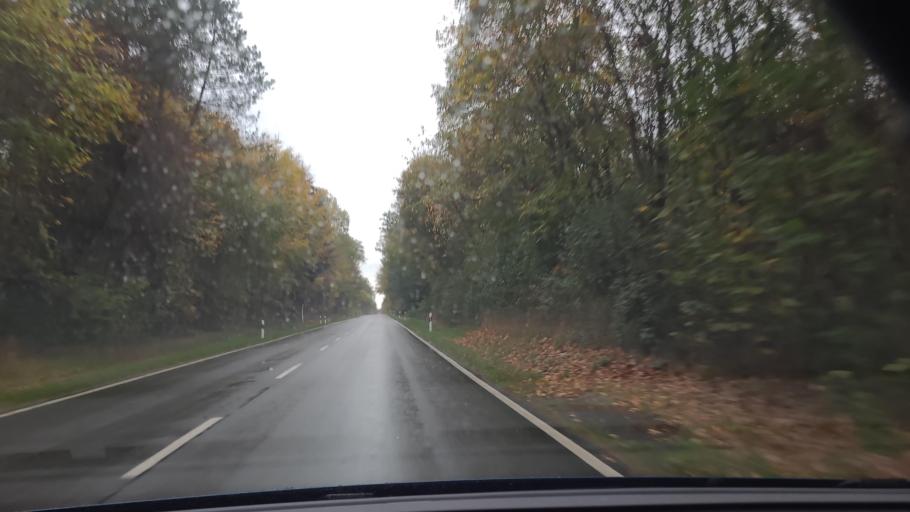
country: LU
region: Luxembourg
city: Bereldange
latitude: 49.6370
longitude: 6.1073
